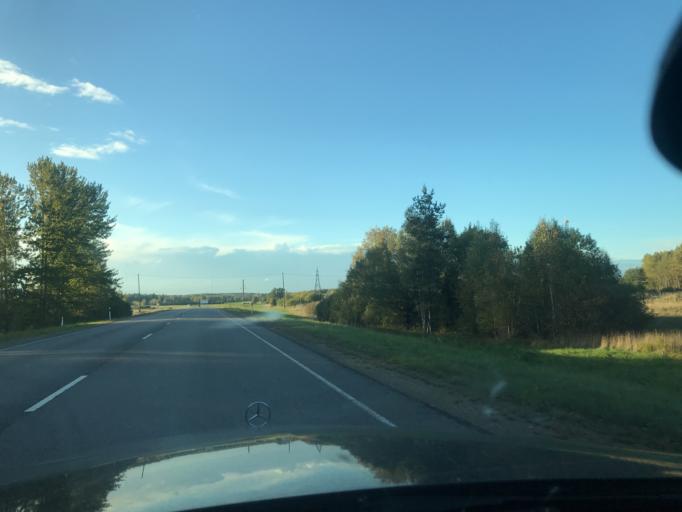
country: EE
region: Vorumaa
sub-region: Voru linn
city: Voru
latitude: 57.8529
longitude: 27.0285
